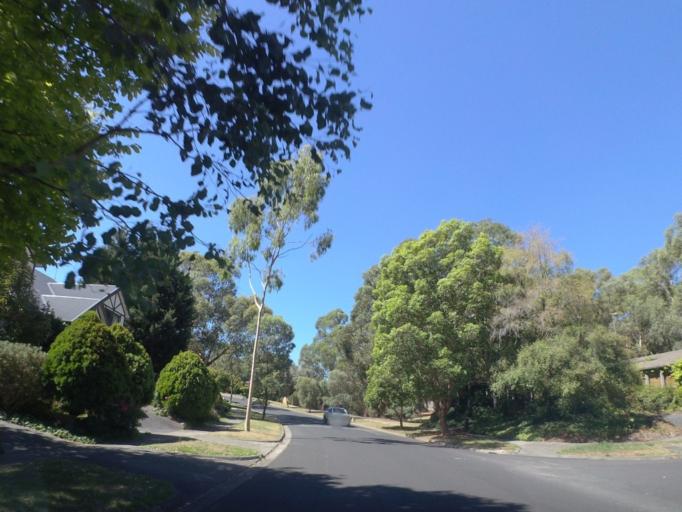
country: AU
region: Victoria
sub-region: Manningham
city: Park Orchards
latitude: -37.7957
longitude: 145.2239
